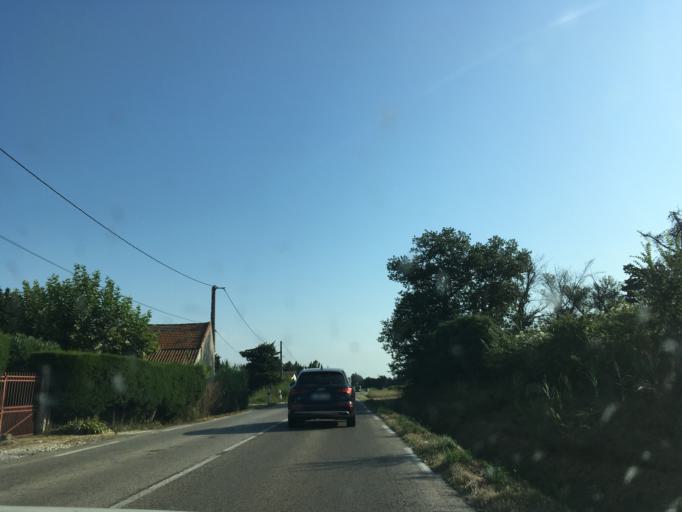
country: FR
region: Languedoc-Roussillon
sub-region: Departement du Gard
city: Fourques
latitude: 43.6553
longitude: 4.5786
